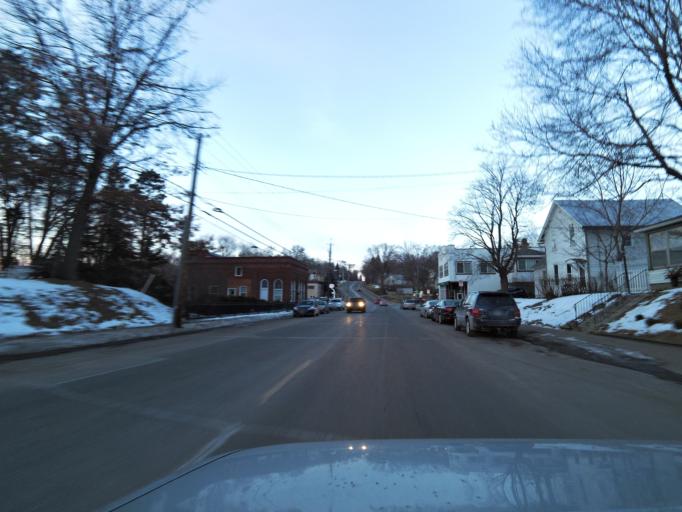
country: US
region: Minnesota
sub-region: Washington County
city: Stillwater
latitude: 45.0593
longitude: -92.8203
